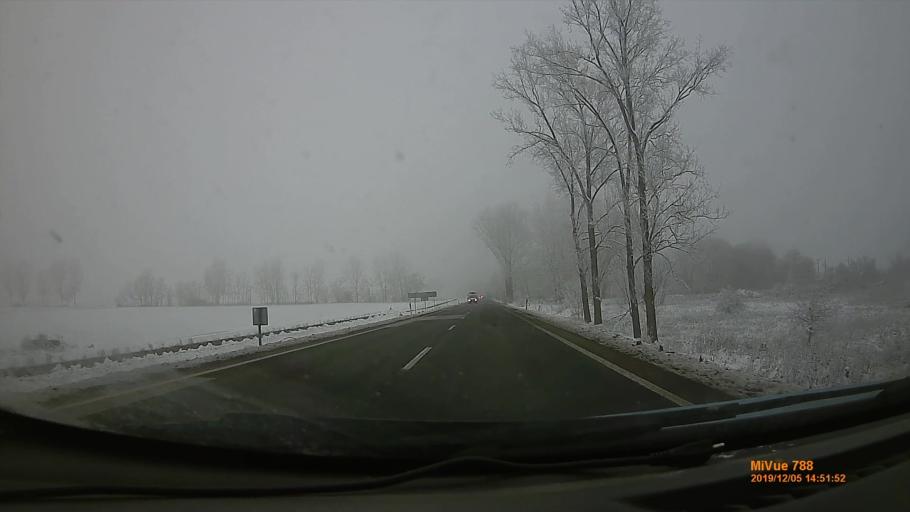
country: HU
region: Szabolcs-Szatmar-Bereg
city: Nyirtelek
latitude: 47.9962
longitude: 21.6516
